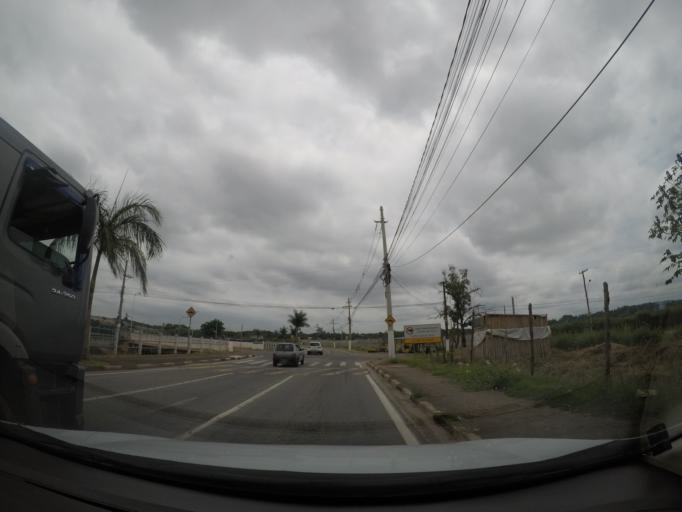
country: BR
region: Sao Paulo
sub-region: Aruja
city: Aruja
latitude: -23.4026
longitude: -46.3630
